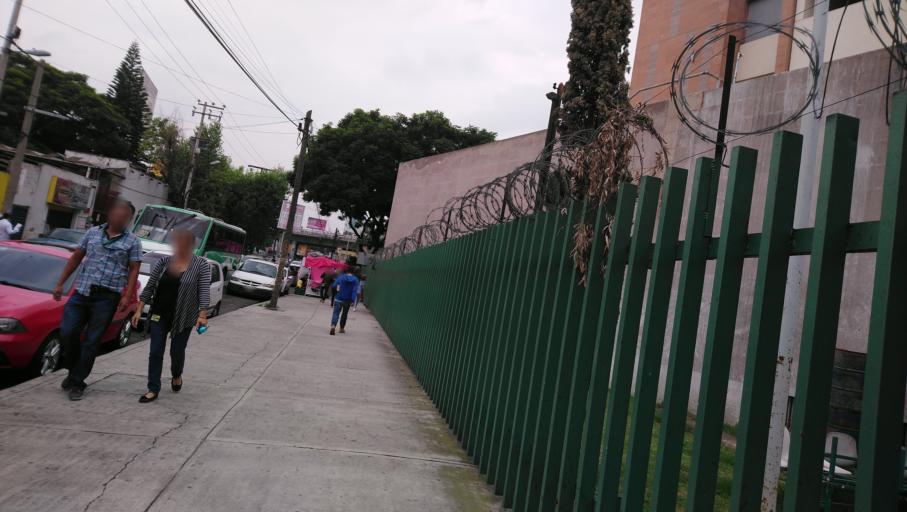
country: MX
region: Mexico City
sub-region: Iztacalco
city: Iztacalco
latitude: 19.4049
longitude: -99.1123
